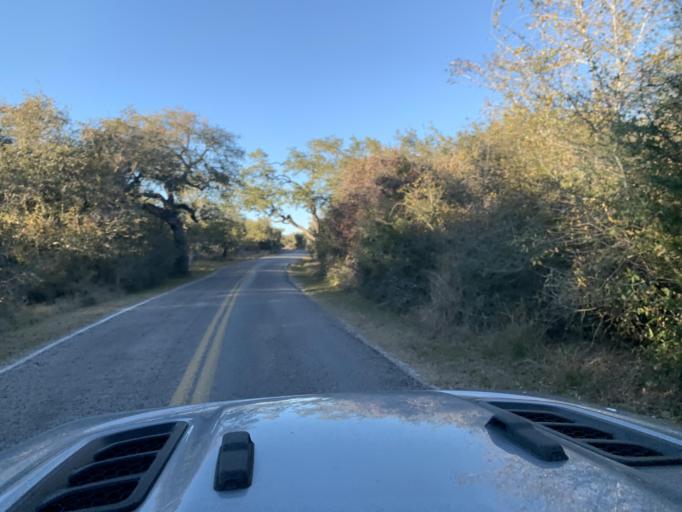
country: US
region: Texas
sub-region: Aransas County
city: Fulton
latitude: 28.1451
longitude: -96.9843
